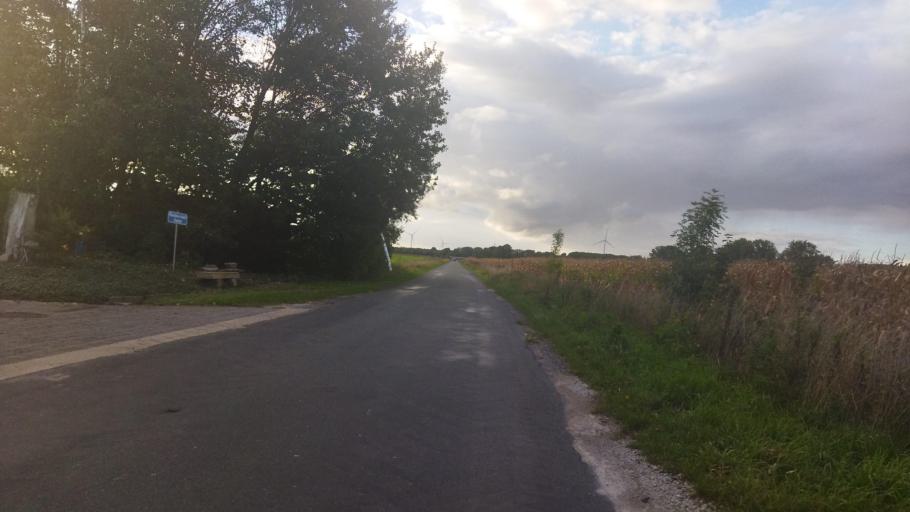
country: DE
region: North Rhine-Westphalia
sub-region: Regierungsbezirk Munster
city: Billerbeck
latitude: 51.9765
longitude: 7.2398
